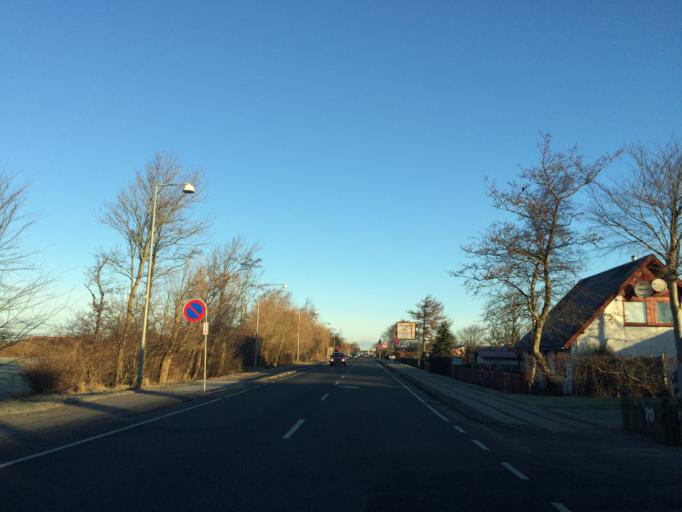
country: DK
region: Central Jutland
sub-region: Lemvig Kommune
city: Lemvig
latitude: 56.4167
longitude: 8.3075
